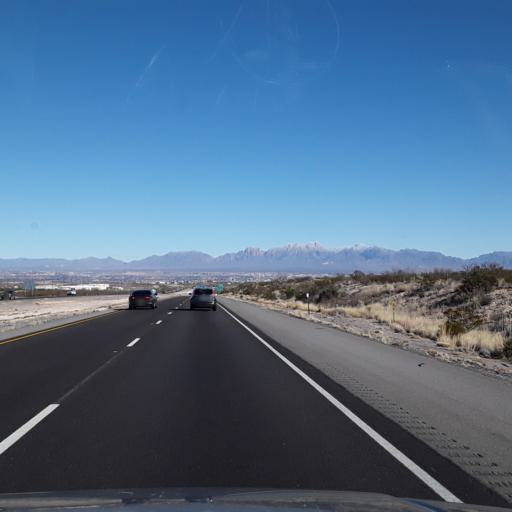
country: US
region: New Mexico
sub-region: Dona Ana County
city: Mesilla
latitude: 32.2746
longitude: -106.9044
